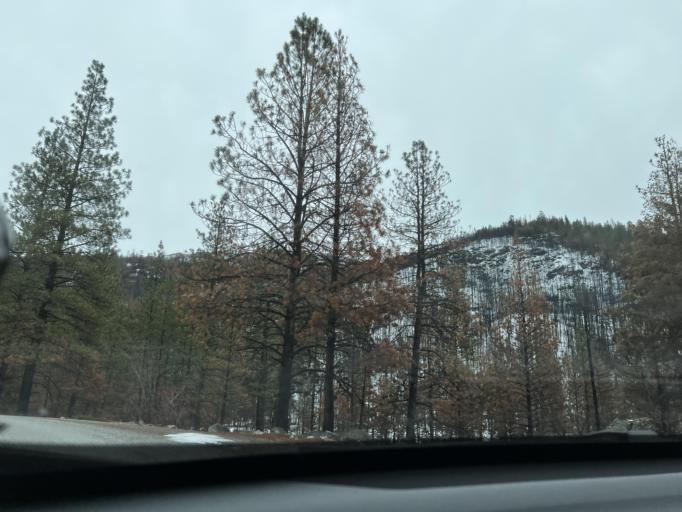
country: US
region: Washington
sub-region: Okanogan County
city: Brewster
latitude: 48.5788
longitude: -120.1598
